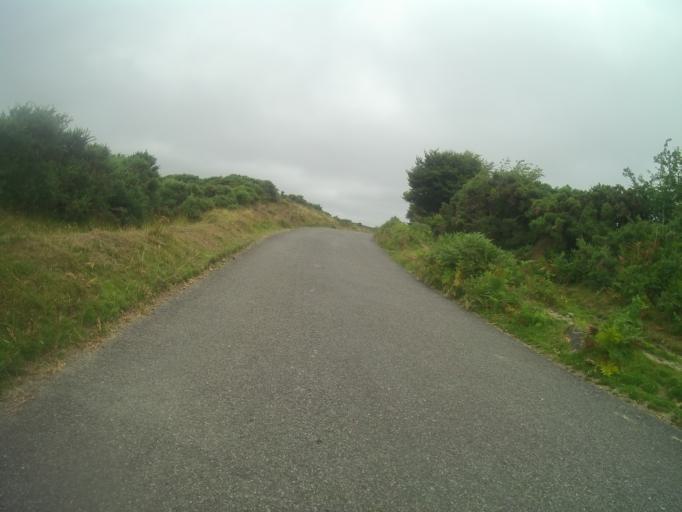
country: GB
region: England
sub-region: Devon
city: Buckfastleigh
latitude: 50.5169
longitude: -3.8439
